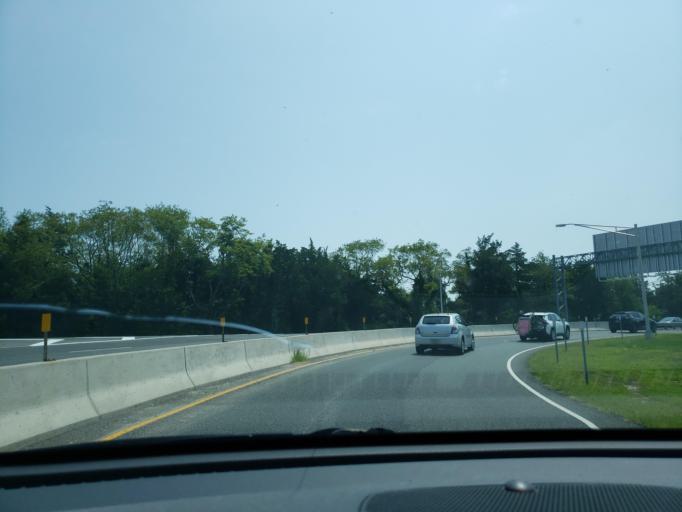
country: US
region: New Jersey
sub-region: Cape May County
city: Erma
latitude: 38.9612
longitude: -74.9033
